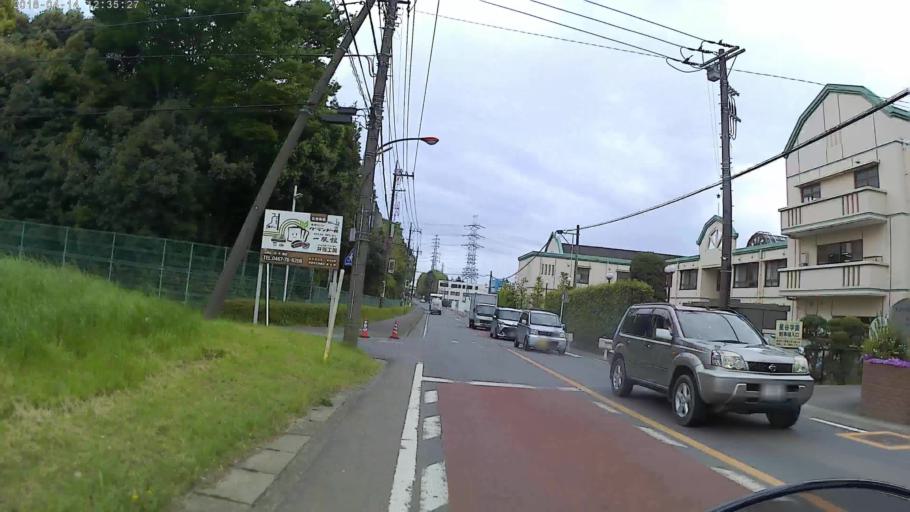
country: JP
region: Kanagawa
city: Atsugi
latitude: 35.4208
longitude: 139.4087
